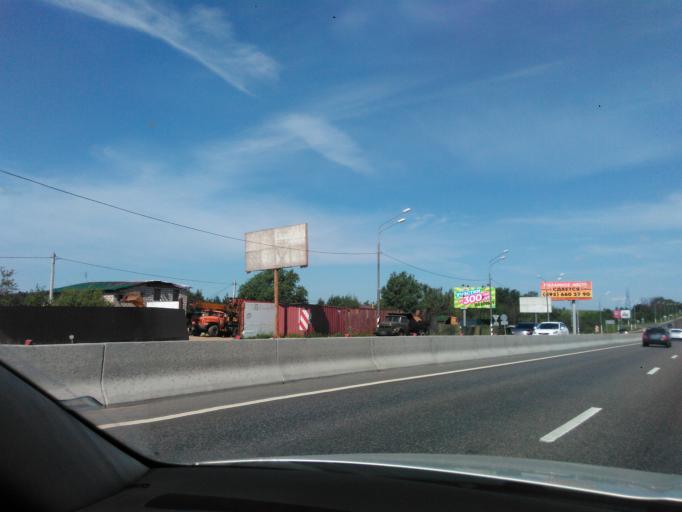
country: RU
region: Moskovskaya
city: Lozhki
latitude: 56.1068
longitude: 37.0946
